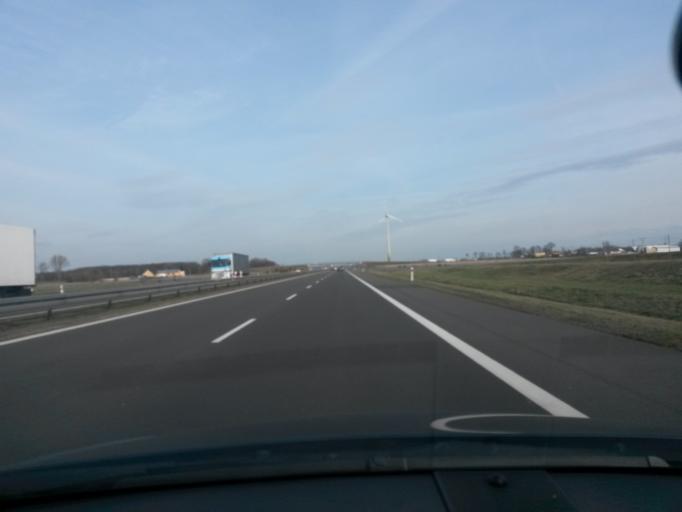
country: PL
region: Greater Poland Voivodeship
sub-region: Powiat sredzki
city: Sroda Wielkopolska
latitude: 52.3101
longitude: 17.2616
